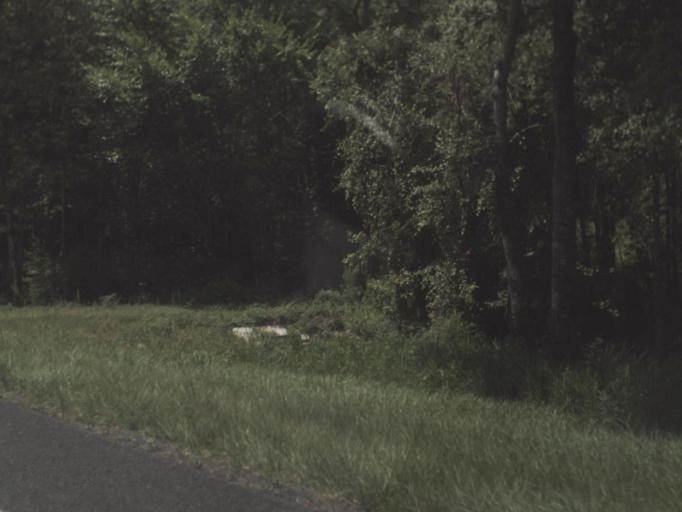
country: US
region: Florida
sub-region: Taylor County
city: Perry
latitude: 30.2390
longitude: -83.6900
